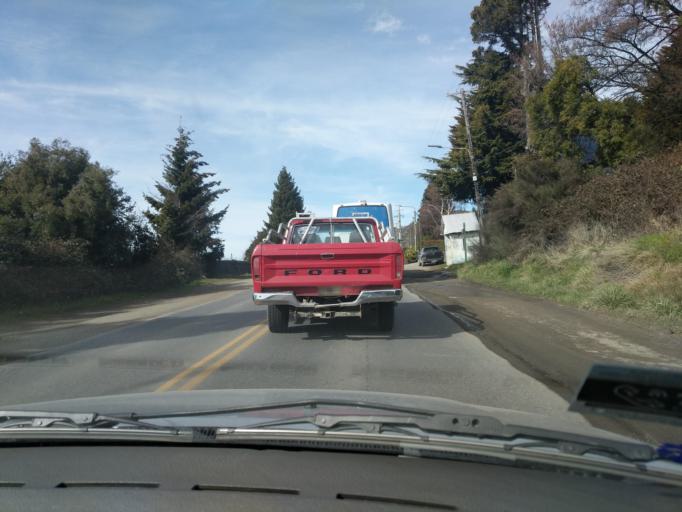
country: AR
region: Rio Negro
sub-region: Departamento de Bariloche
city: San Carlos de Bariloche
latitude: -41.1292
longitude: -71.3482
